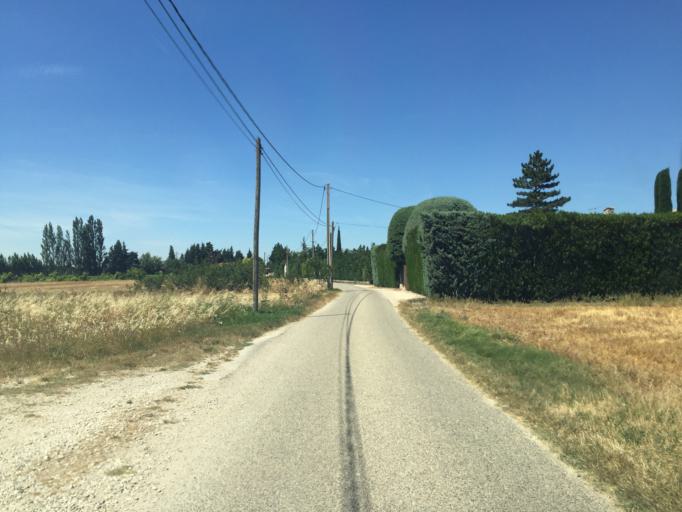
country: FR
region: Provence-Alpes-Cote d'Azur
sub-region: Departement du Vaucluse
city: Bedarrides
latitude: 44.0461
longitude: 4.9084
